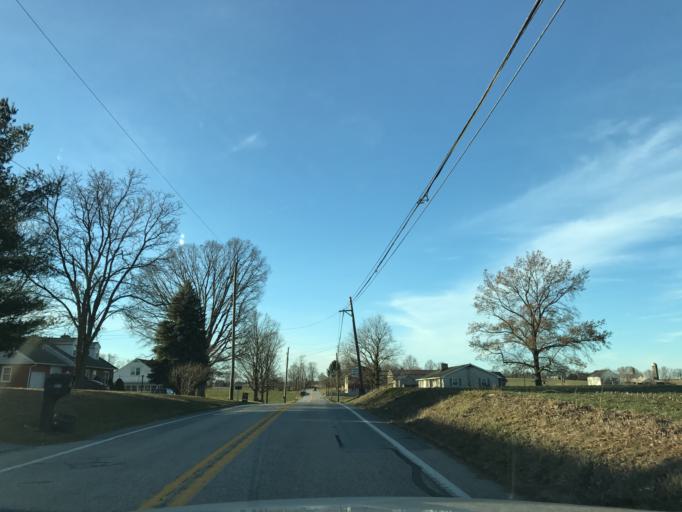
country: US
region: Pennsylvania
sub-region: Lancaster County
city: Maytown
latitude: 40.0815
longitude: -76.5877
